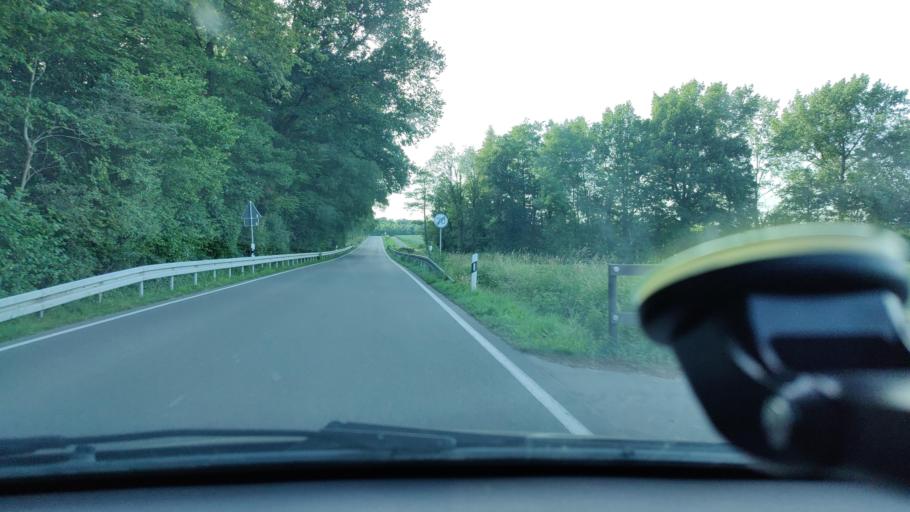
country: DE
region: North Rhine-Westphalia
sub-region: Regierungsbezirk Munster
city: Billerbeck
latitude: 51.9988
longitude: 7.2286
